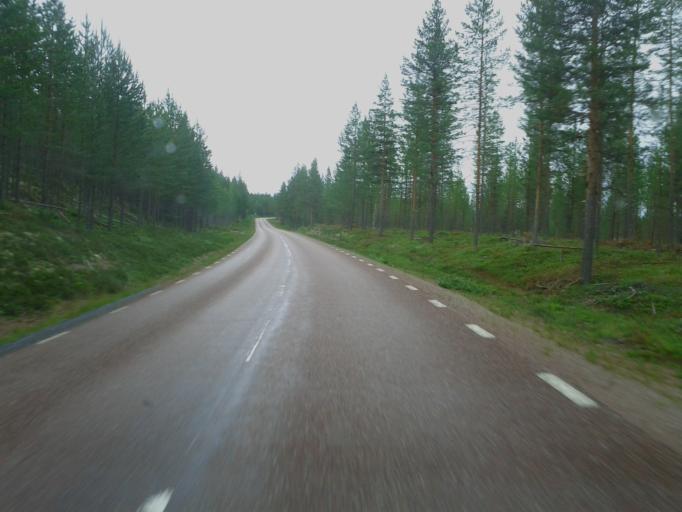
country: NO
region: Hedmark
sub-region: Trysil
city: Innbygda
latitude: 61.7920
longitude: 12.9248
